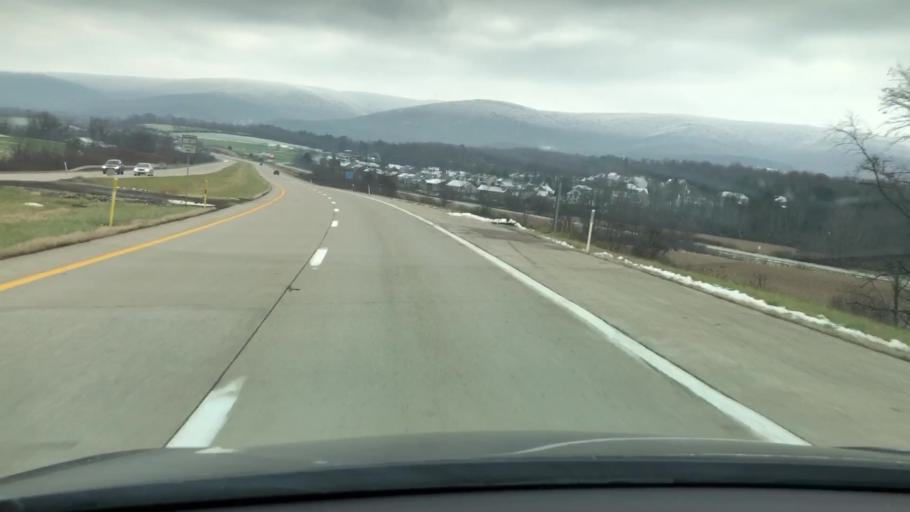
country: US
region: Pennsylvania
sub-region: Fayette County
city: Leith-Hatfield
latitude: 39.8673
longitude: -79.7362
